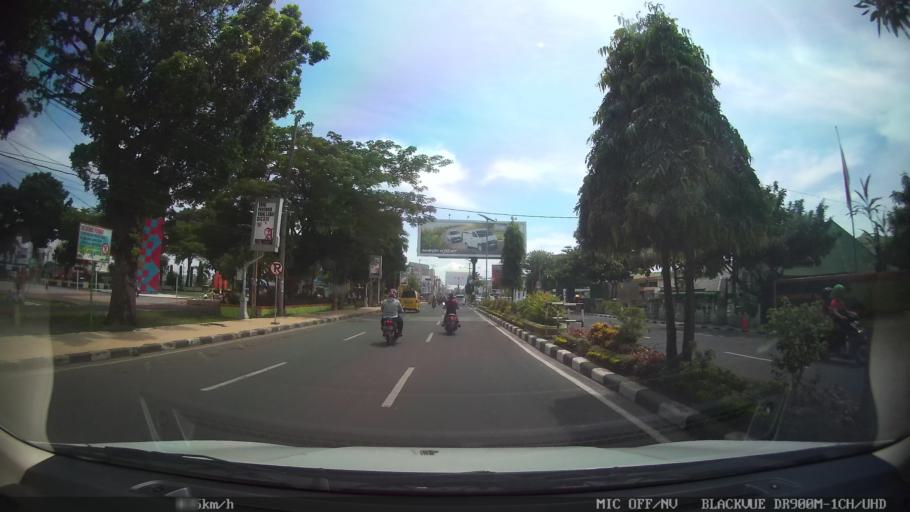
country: ID
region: North Sumatra
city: Binjai
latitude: 3.6028
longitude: 98.4819
